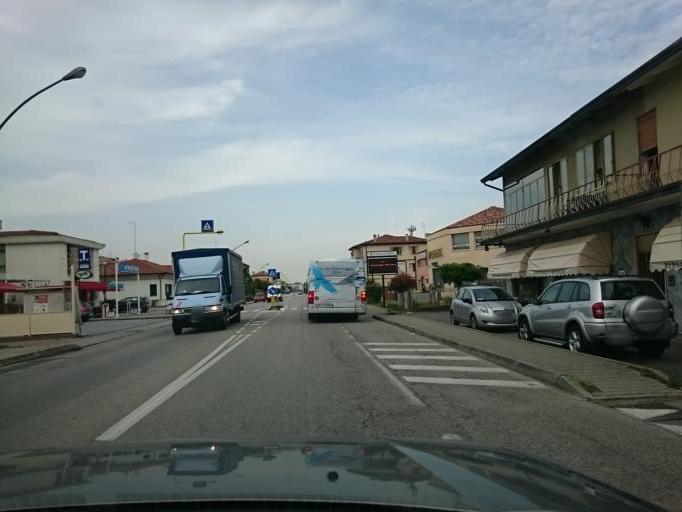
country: IT
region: Veneto
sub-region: Provincia di Venezia
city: Mira Taglio
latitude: 45.4361
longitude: 12.1305
